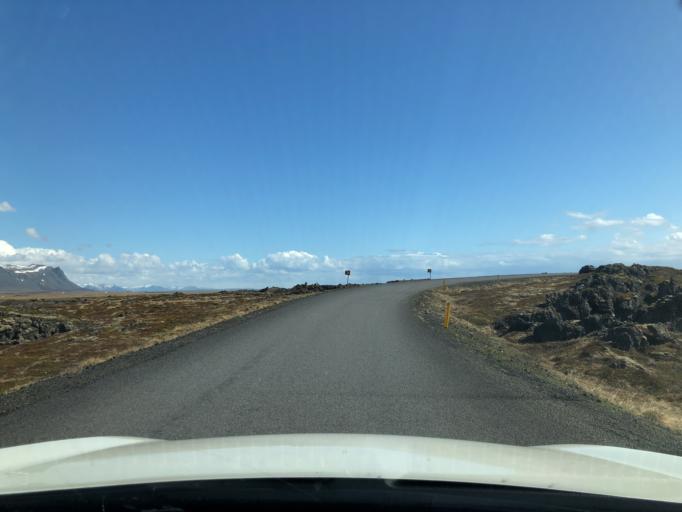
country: IS
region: West
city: Olafsvik
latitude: 64.8265
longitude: -23.3960
